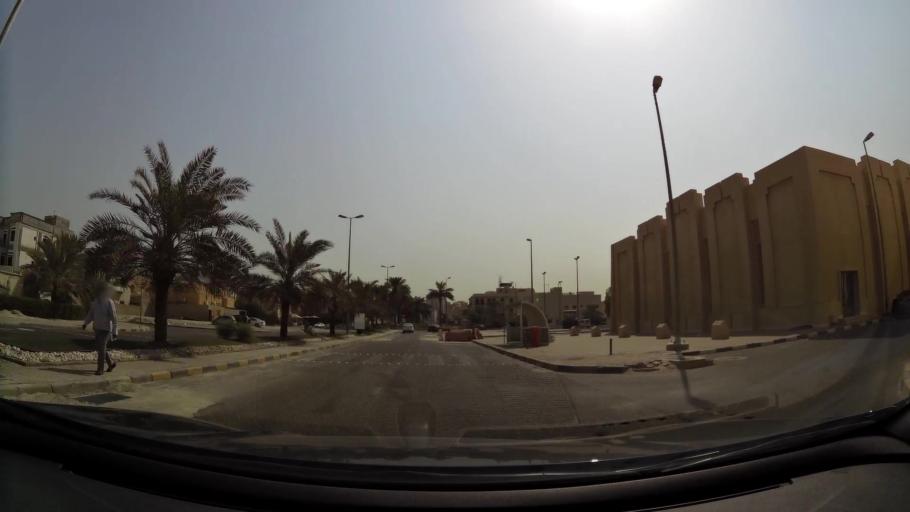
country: KW
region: Al Asimah
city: Ad Dasmah
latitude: 29.3496
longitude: 48.0049
